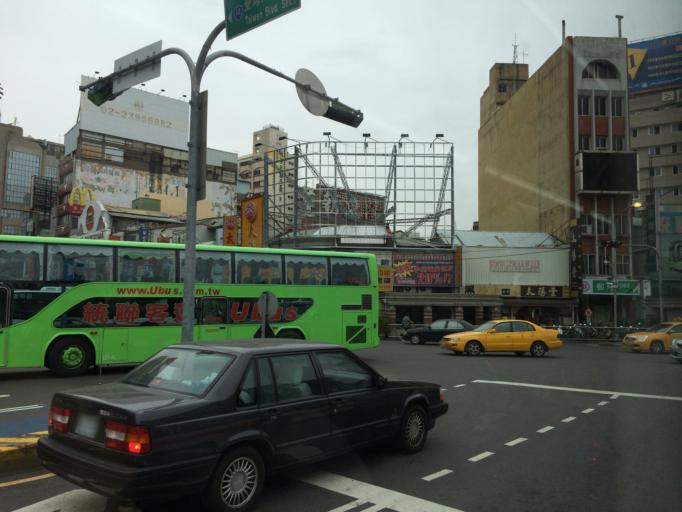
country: TW
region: Taiwan
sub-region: Taichung City
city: Taichung
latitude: 24.1374
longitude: 120.6847
